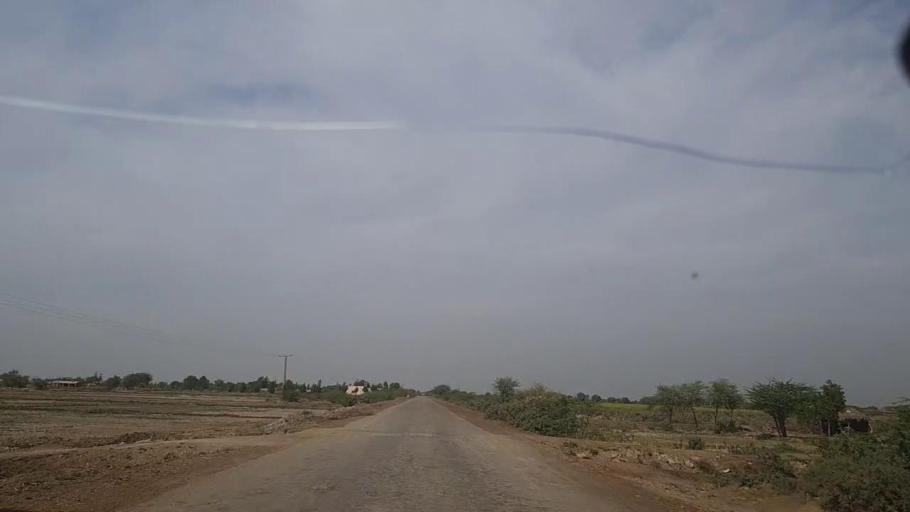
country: PK
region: Sindh
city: Pithoro
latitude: 25.5617
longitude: 69.3629
